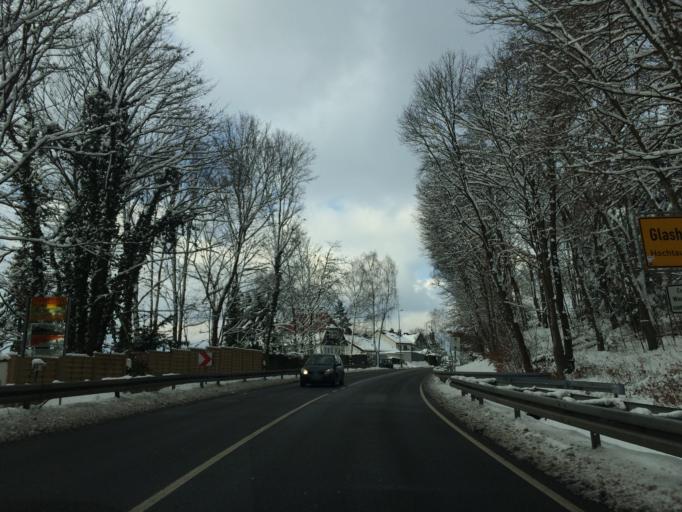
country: DE
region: Hesse
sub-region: Regierungsbezirk Darmstadt
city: Glashutten
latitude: 50.2133
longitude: 8.4045
